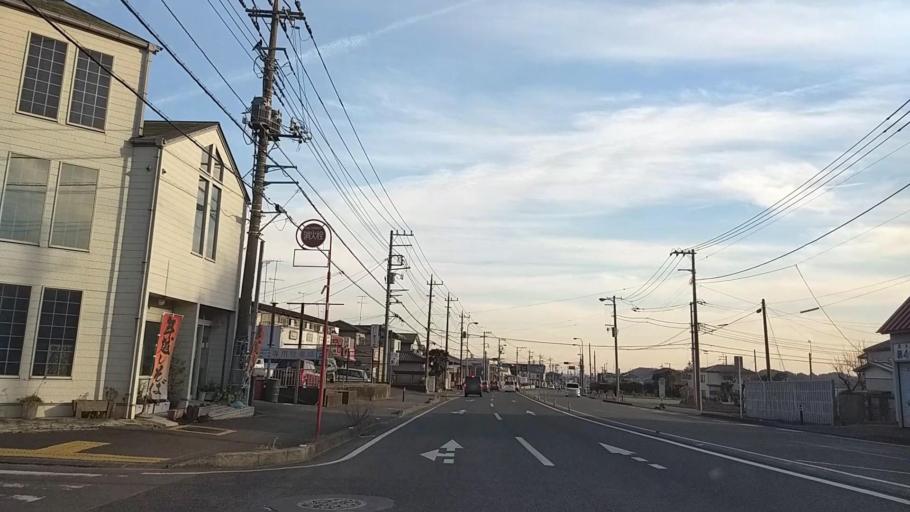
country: JP
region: Kanagawa
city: Atsugi
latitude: 35.4918
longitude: 139.3216
